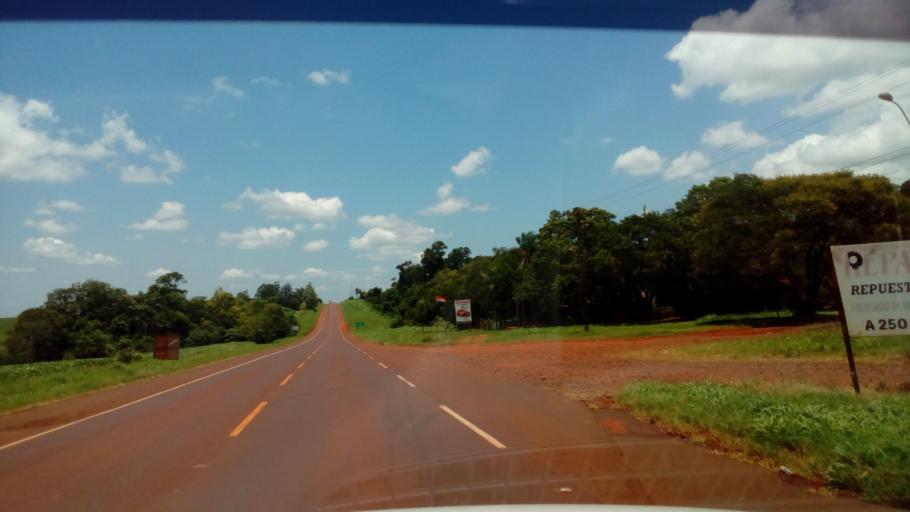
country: PY
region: Itapua
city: Arquitecto Tomas Romero Pereira
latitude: -26.3723
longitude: -55.2377
